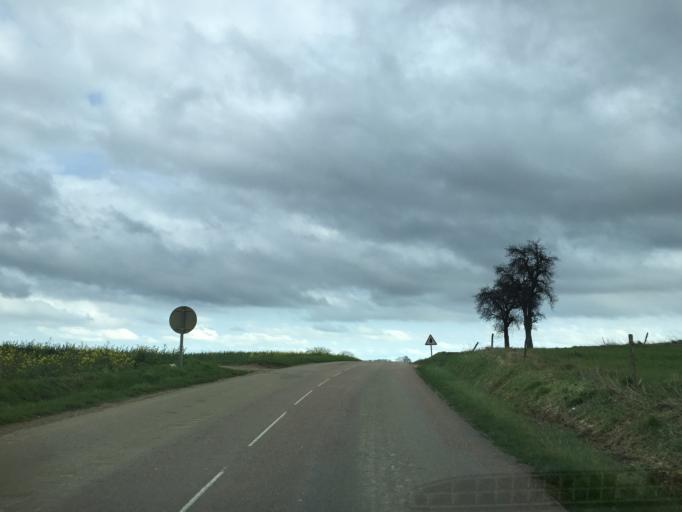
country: FR
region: Bourgogne
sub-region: Departement de l'Yonne
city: Pourrain
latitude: 47.8004
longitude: 3.4249
